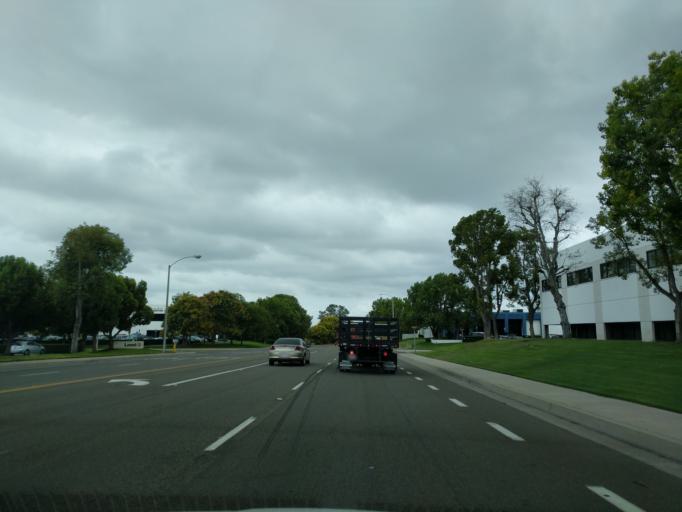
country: US
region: California
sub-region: Orange County
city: Lake Forest
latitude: 33.6443
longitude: -117.7216
